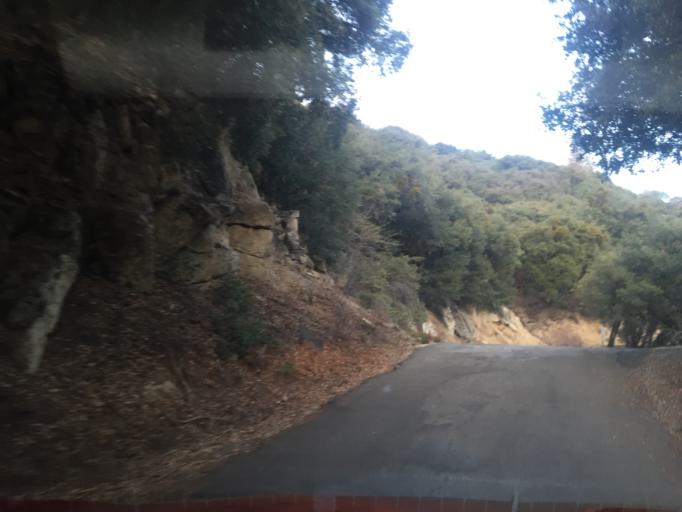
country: US
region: California
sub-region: Tulare County
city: Three Rivers
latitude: 36.4454
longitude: -118.7150
